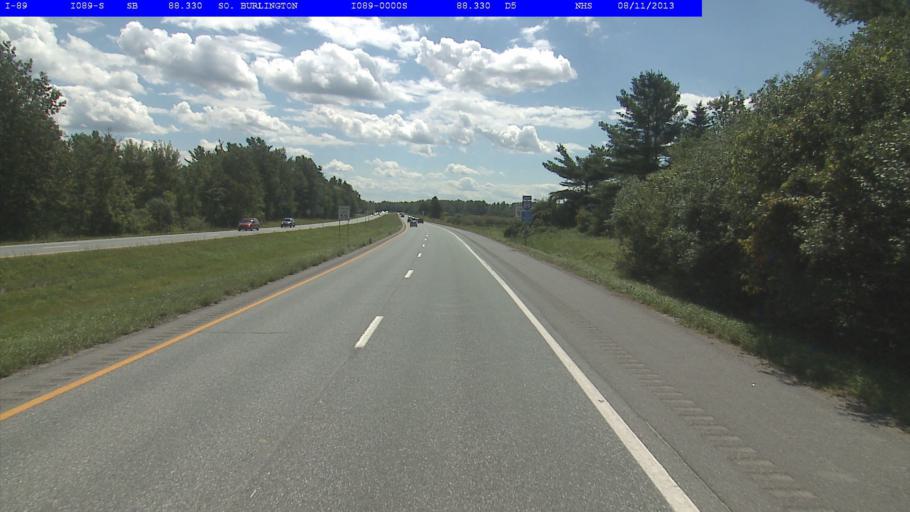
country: US
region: Vermont
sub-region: Chittenden County
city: South Burlington
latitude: 44.4643
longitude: -73.1858
